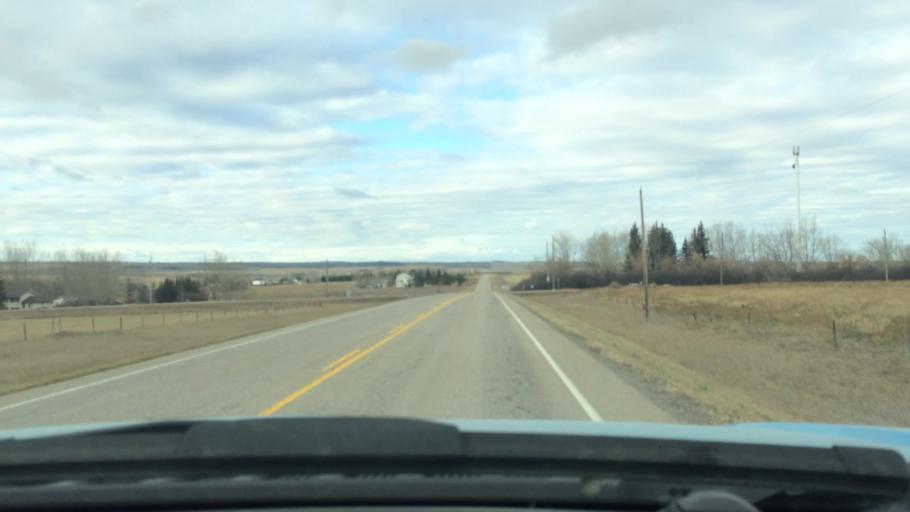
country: CA
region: Alberta
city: Airdrie
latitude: 51.2123
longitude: -114.1388
